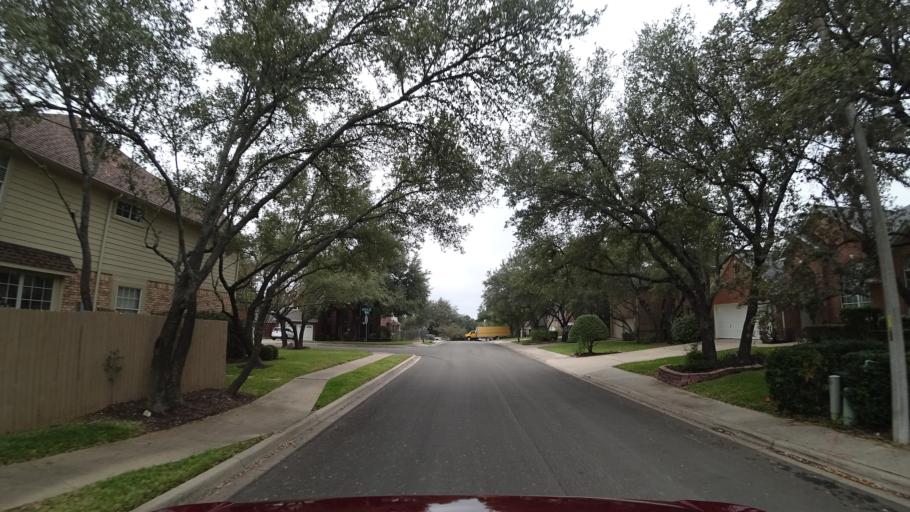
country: US
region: Texas
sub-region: Williamson County
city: Anderson Mill
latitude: 30.4376
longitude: -97.8291
